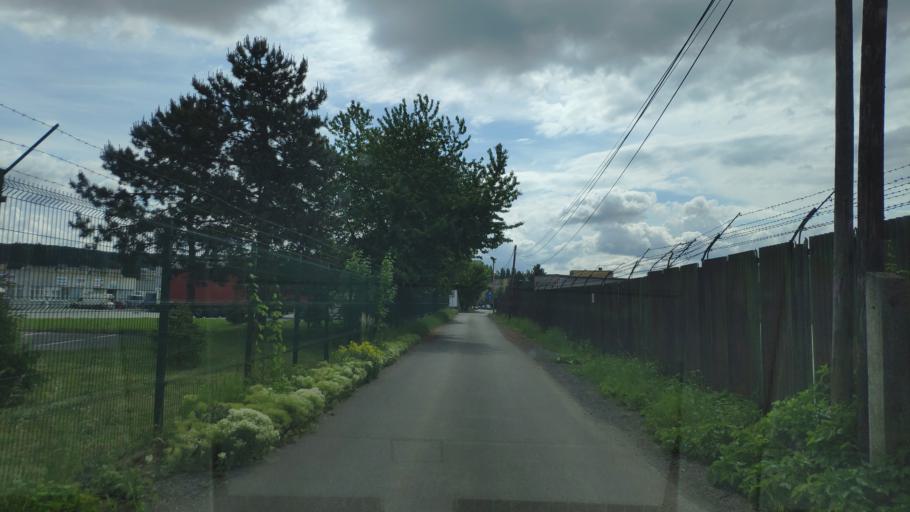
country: SK
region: Kosicky
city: Kosice
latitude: 48.6871
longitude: 21.2760
